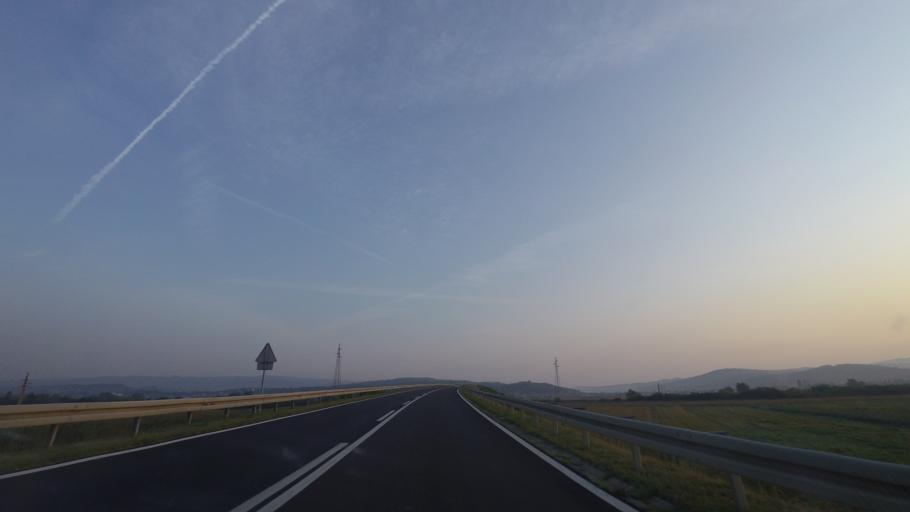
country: HR
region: Brodsko-Posavska
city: Nova Gradiska
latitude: 45.2449
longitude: 17.4081
